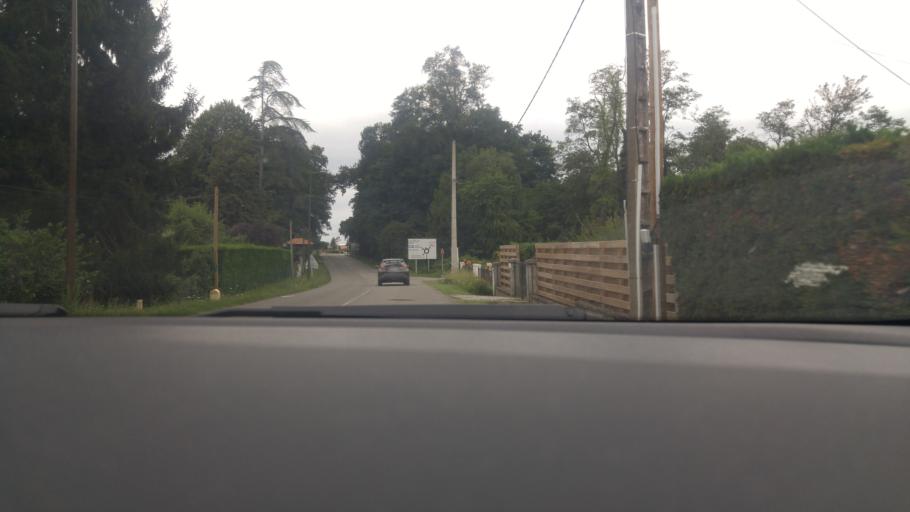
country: FR
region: Aquitaine
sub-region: Departement des Landes
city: Soustons
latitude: 43.7471
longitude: -1.3162
